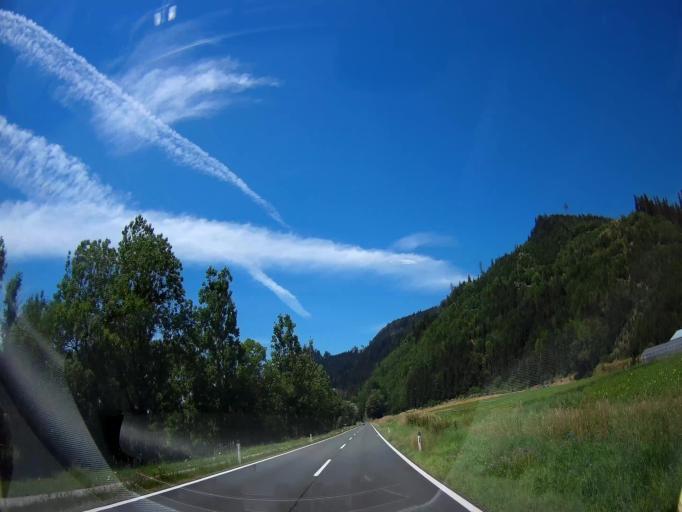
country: AT
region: Carinthia
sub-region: Politischer Bezirk Sankt Veit an der Glan
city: Micheldorf
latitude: 46.9018
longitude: 14.4108
